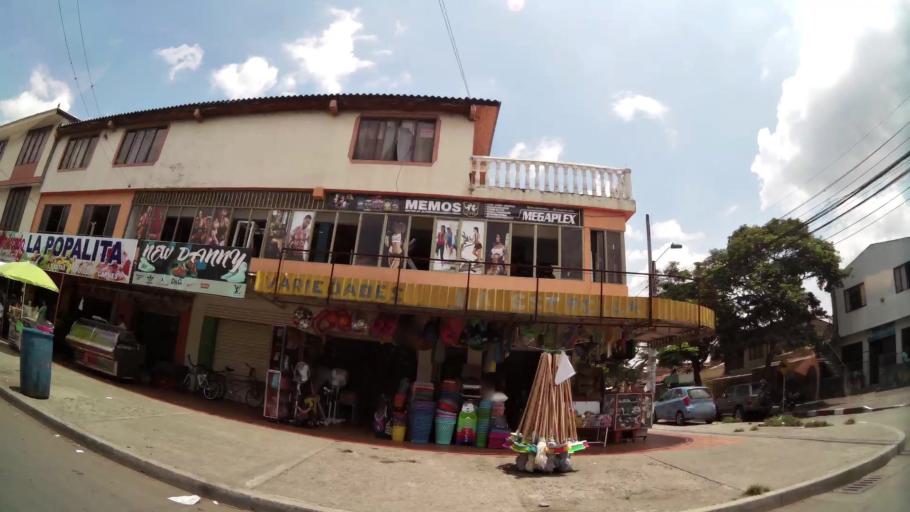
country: CO
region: Valle del Cauca
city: Cali
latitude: 3.4547
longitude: -76.4804
